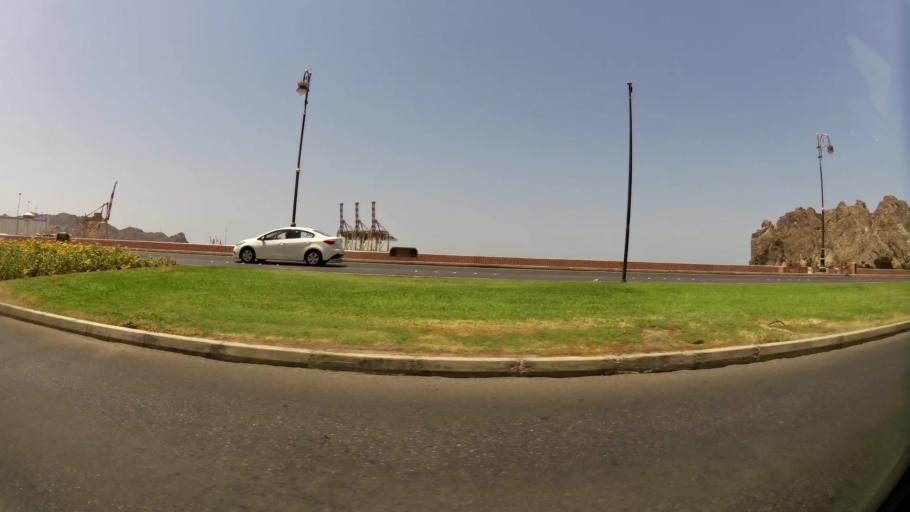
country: OM
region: Muhafazat Masqat
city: Muscat
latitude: 23.6223
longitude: 58.5721
